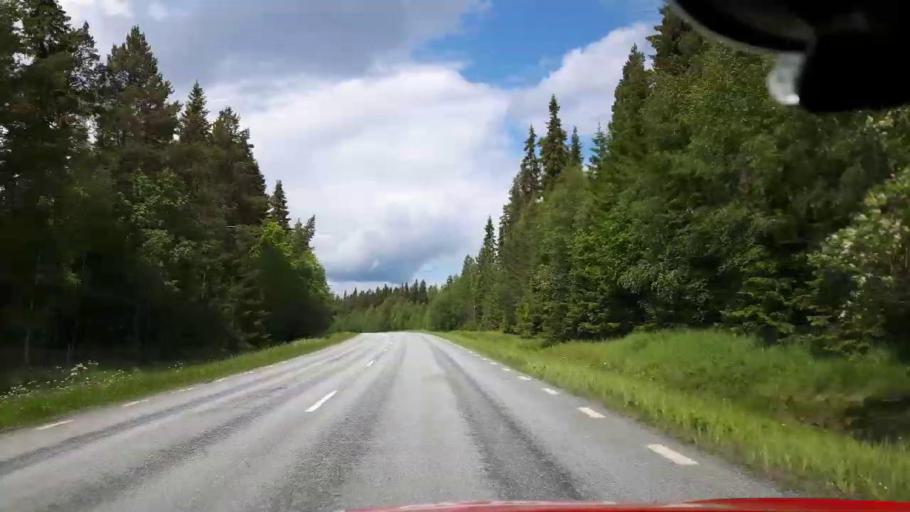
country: SE
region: Jaemtland
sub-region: Krokoms Kommun
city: Krokom
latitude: 63.3783
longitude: 14.3841
